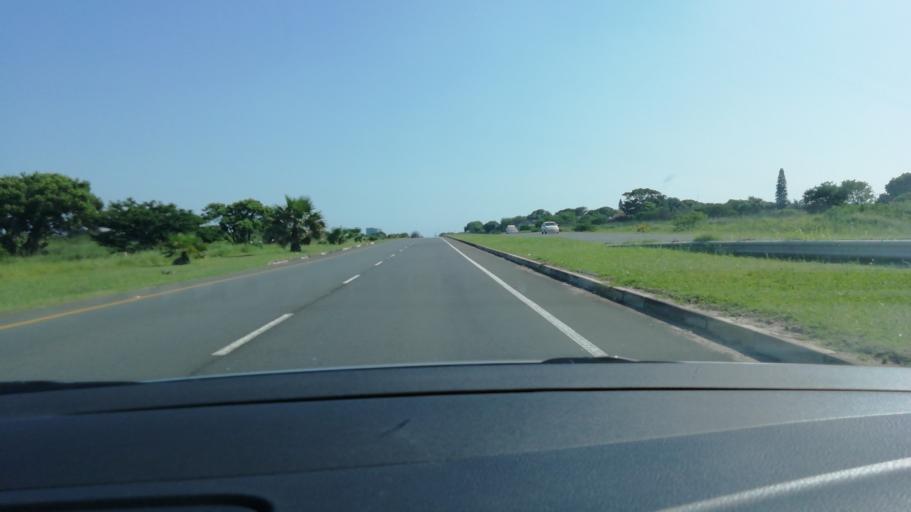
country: ZA
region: KwaZulu-Natal
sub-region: uThungulu District Municipality
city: Richards Bay
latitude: -28.7653
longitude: 32.0485
